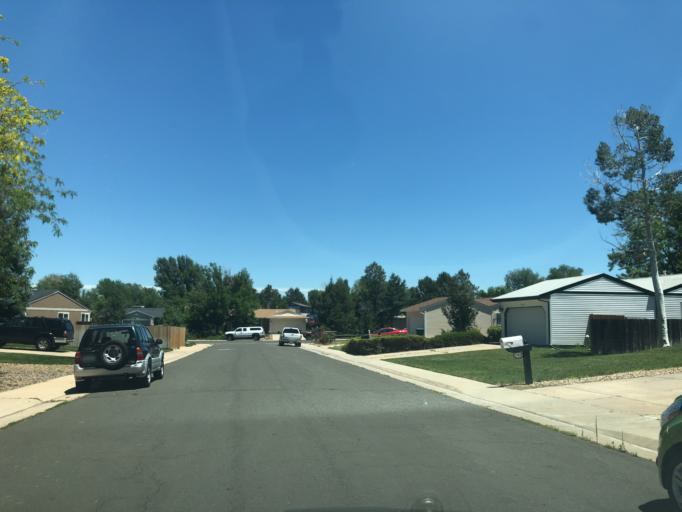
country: US
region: Colorado
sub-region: Arapahoe County
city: Dove Valley
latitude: 39.6196
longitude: -104.7799
